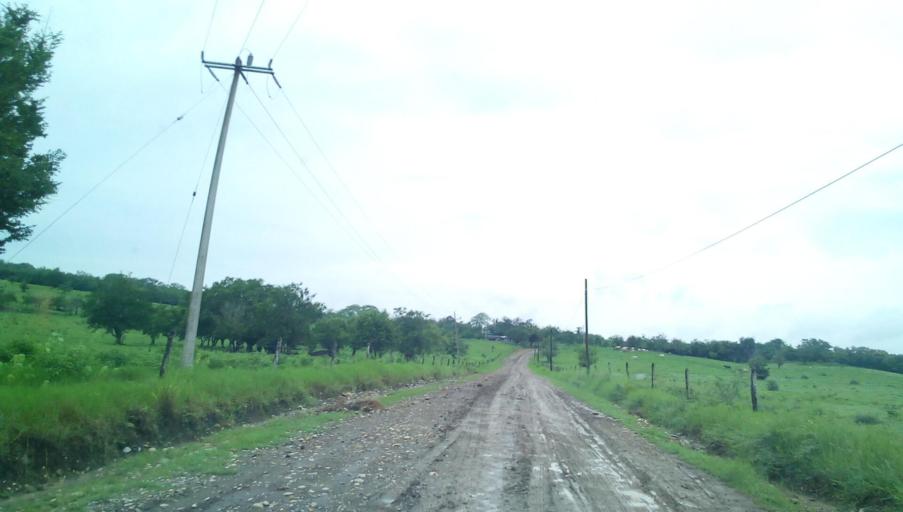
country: MX
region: Veracruz
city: Tempoal de Sanchez
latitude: 21.4368
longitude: -98.4230
